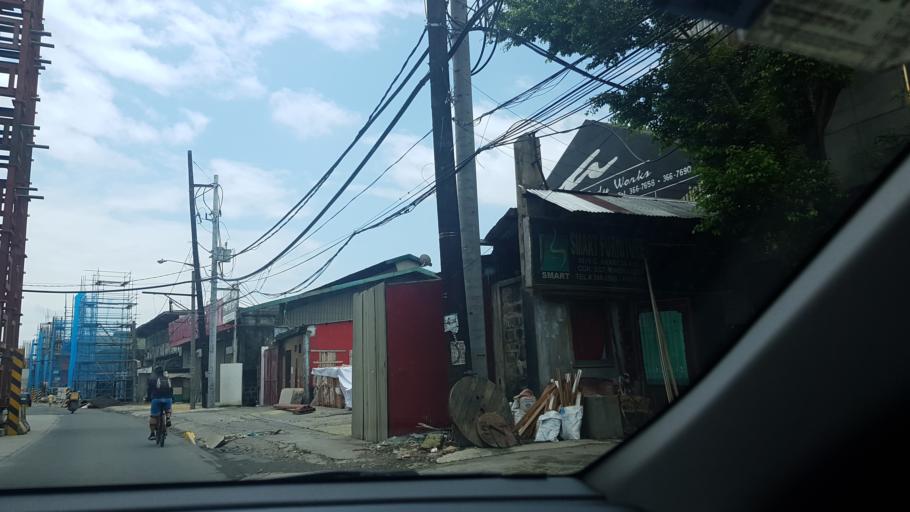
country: PH
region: Calabarzon
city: Del Monte
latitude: 14.6434
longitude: 121.0057
